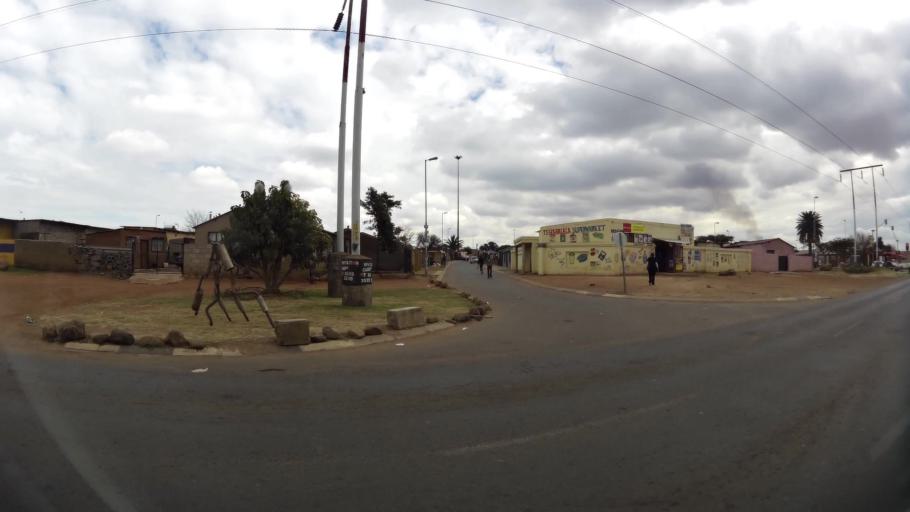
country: ZA
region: Gauteng
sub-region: City of Johannesburg Metropolitan Municipality
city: Soweto
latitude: -26.2682
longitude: 27.8606
